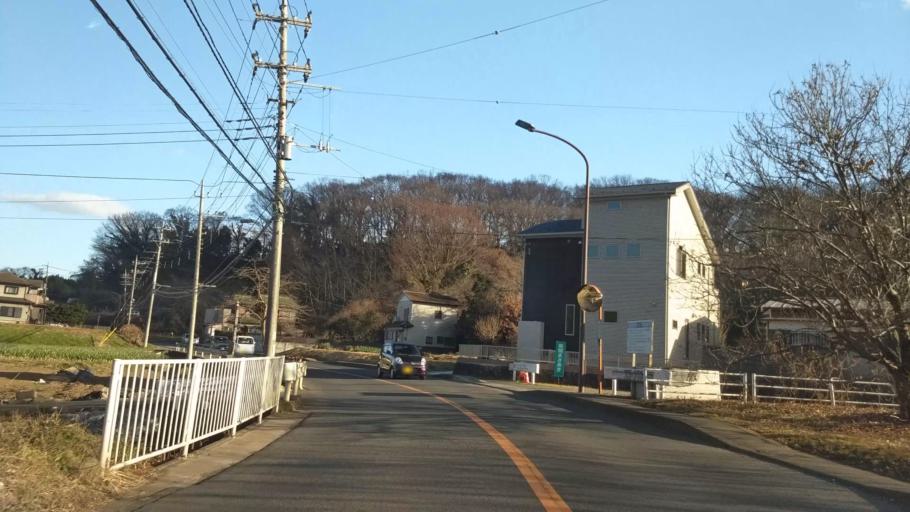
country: JP
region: Kanagawa
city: Oiso
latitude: 35.3435
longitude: 139.2838
